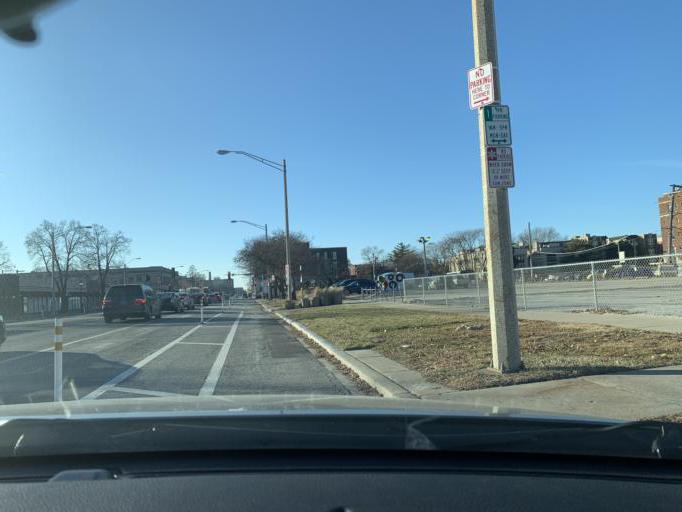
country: US
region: Illinois
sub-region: Cook County
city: Oak Park
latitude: 41.8799
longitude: -87.7929
